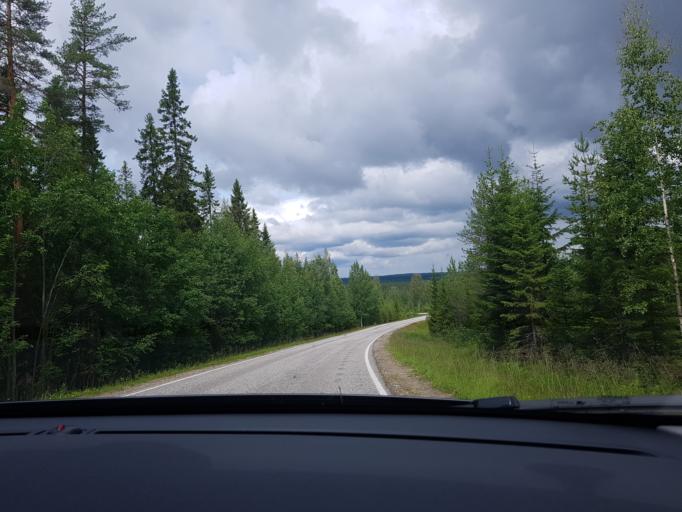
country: FI
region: Kainuu
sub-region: Kehys-Kainuu
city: Kuhmo
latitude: 64.2555
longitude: 29.3884
